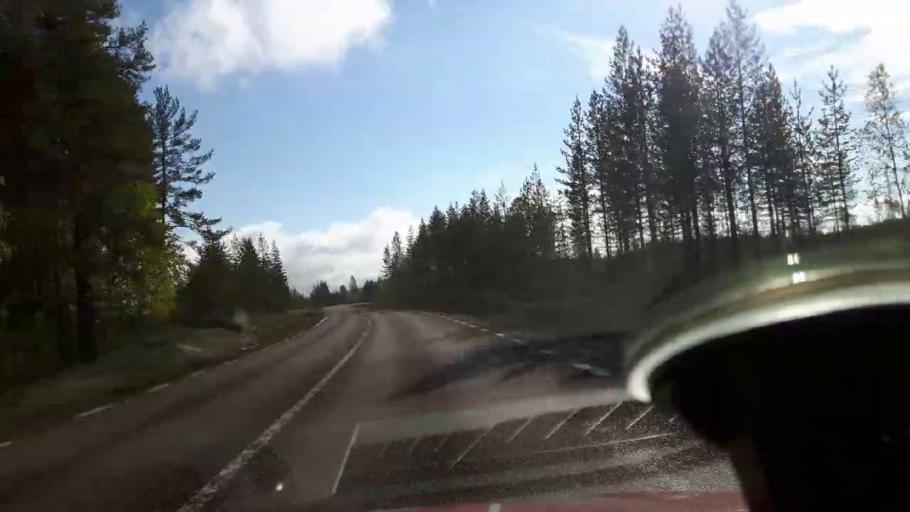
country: SE
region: Gaevleborg
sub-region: Ljusdals Kommun
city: Farila
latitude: 61.9011
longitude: 15.6426
